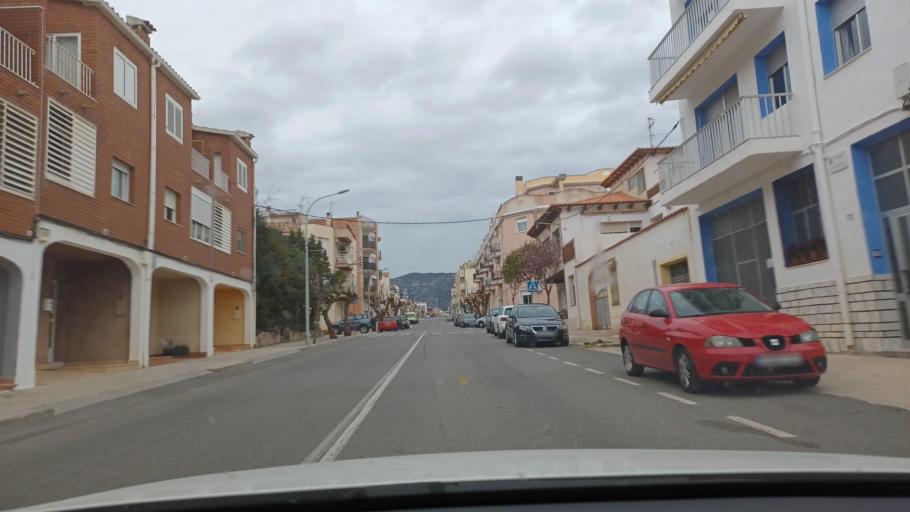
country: ES
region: Valencia
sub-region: Provincia de Castello
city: Rosell
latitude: 40.6314
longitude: 0.2871
